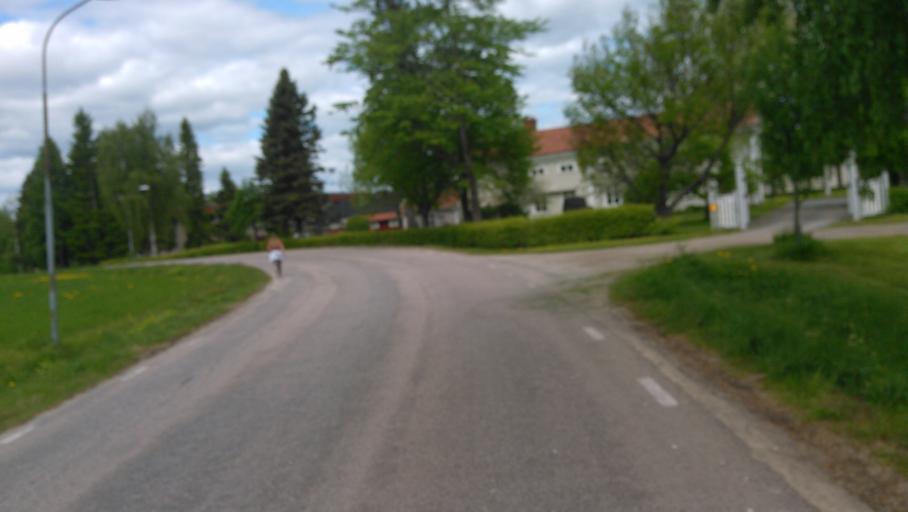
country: SE
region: Vaesterbotten
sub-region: Umea Kommun
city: Roback
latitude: 63.8716
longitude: 20.0655
